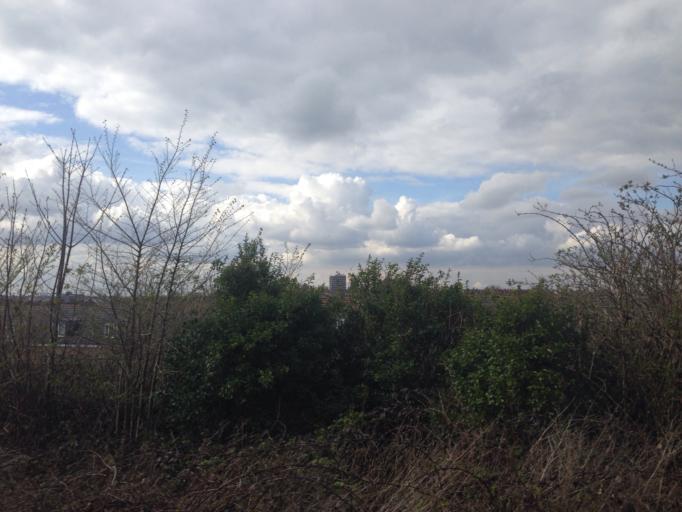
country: GB
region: England
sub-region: Greater London
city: Mitcham
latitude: 51.4185
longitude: -0.1416
